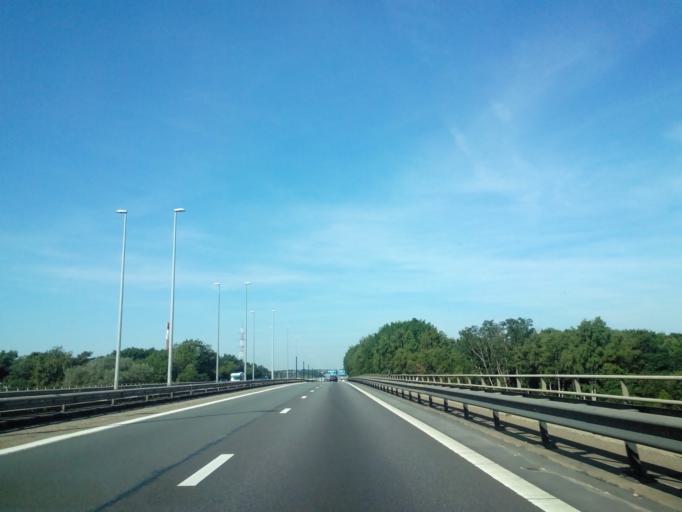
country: BE
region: Flanders
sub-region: Provincie Limburg
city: Beringen
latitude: 51.0014
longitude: 5.2407
